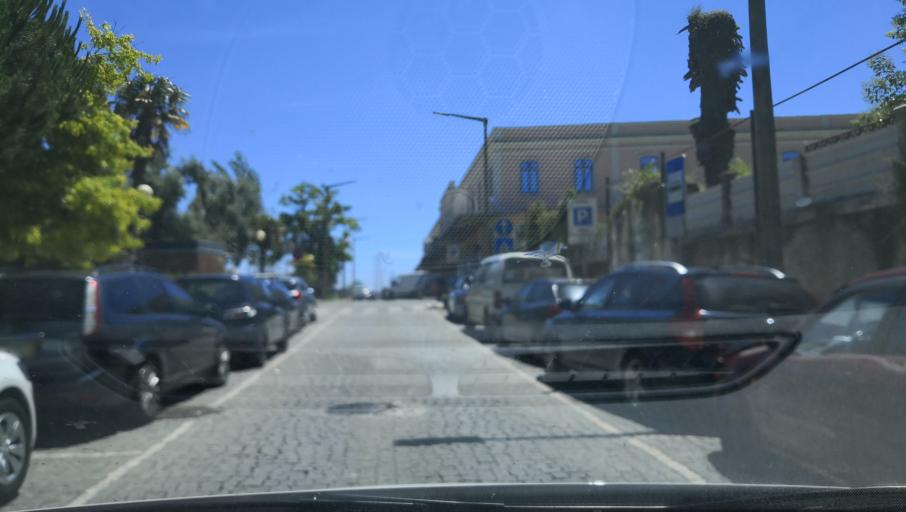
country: PT
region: Coimbra
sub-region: Figueira da Foz
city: Figueira da Foz
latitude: 40.1497
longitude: -8.8616
